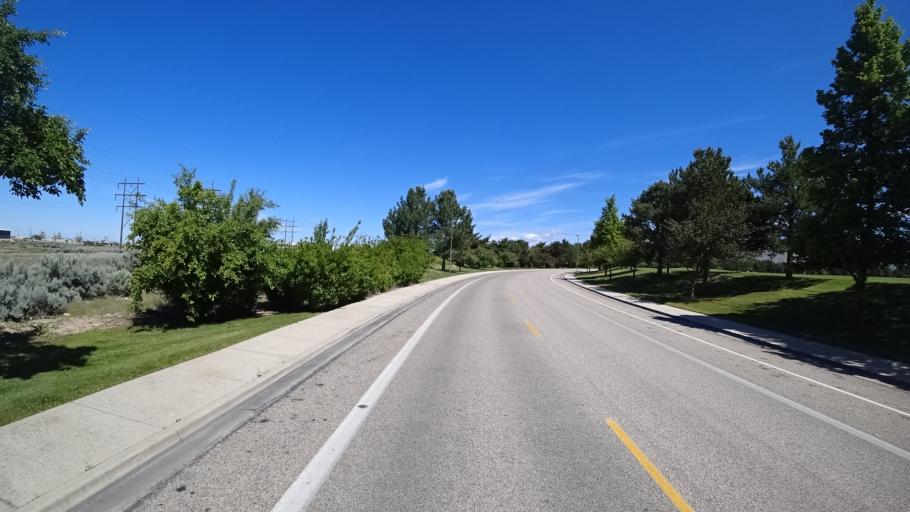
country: US
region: Idaho
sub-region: Ada County
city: Boise
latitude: 43.5478
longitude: -116.1536
